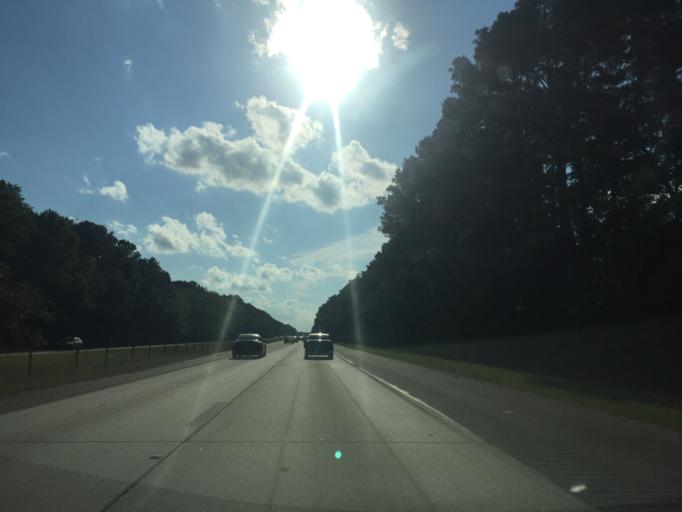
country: US
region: Georgia
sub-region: Chatham County
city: Pooler
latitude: 32.0715
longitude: -81.2158
